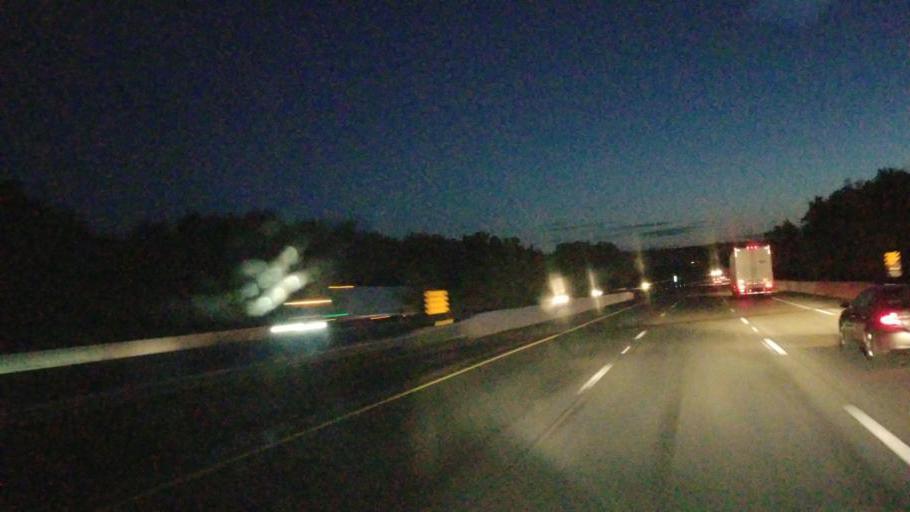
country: US
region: Ohio
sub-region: Richland County
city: Lincoln Heights
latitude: 40.7422
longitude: -82.4530
